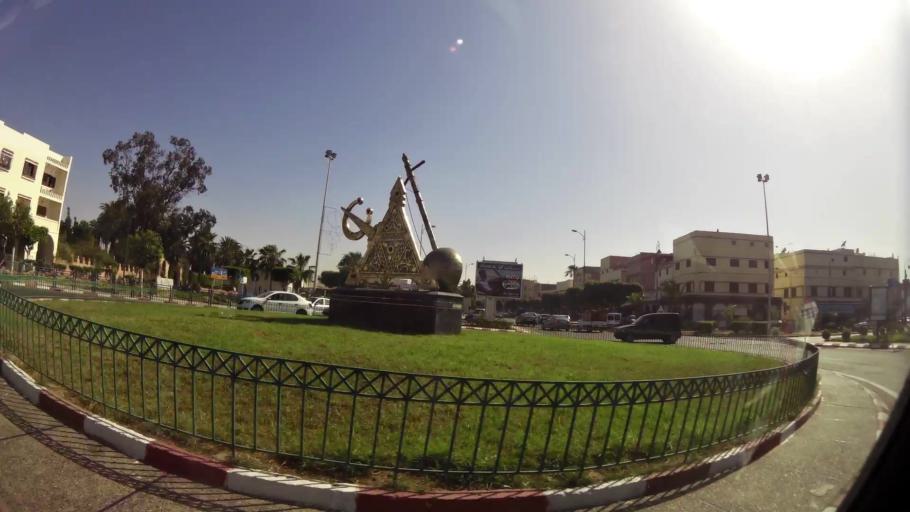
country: MA
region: Souss-Massa-Draa
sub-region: Inezgane-Ait Mellou
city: Inezgane
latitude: 30.3716
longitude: -9.5319
